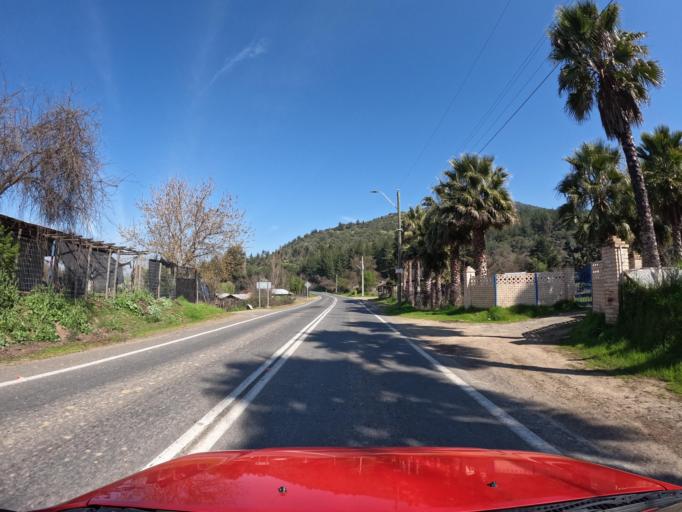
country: CL
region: Maule
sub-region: Provincia de Curico
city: Rauco
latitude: -34.9896
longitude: -71.4382
